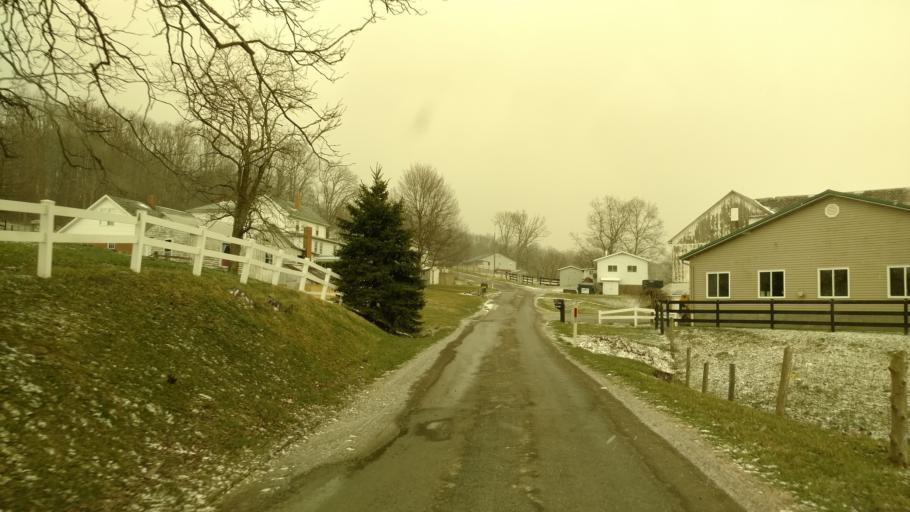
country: US
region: Ohio
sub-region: Coshocton County
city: West Lafayette
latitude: 40.4327
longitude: -81.7961
